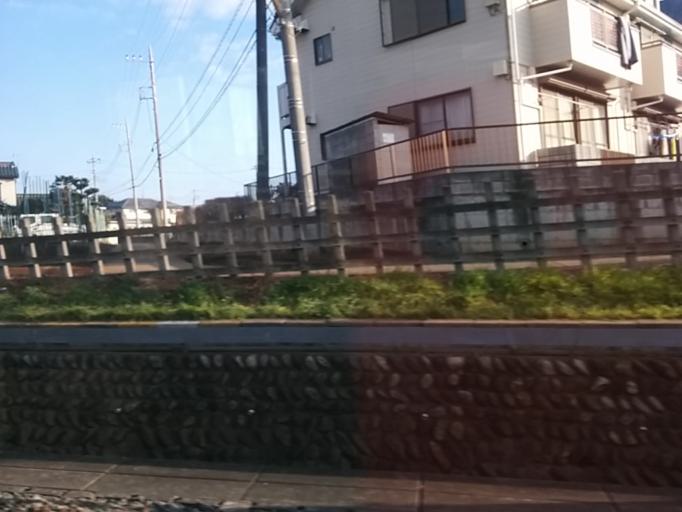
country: JP
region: Saitama
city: Oi
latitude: 35.8532
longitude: 139.5299
